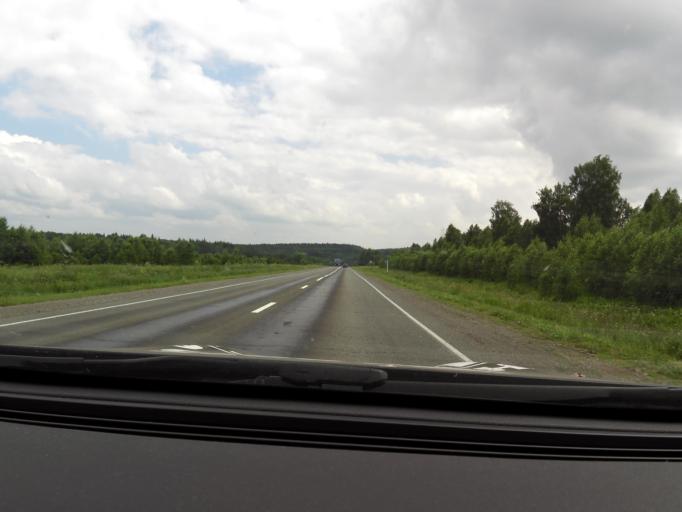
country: RU
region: Perm
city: Suksun
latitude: 56.9316
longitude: 57.5490
